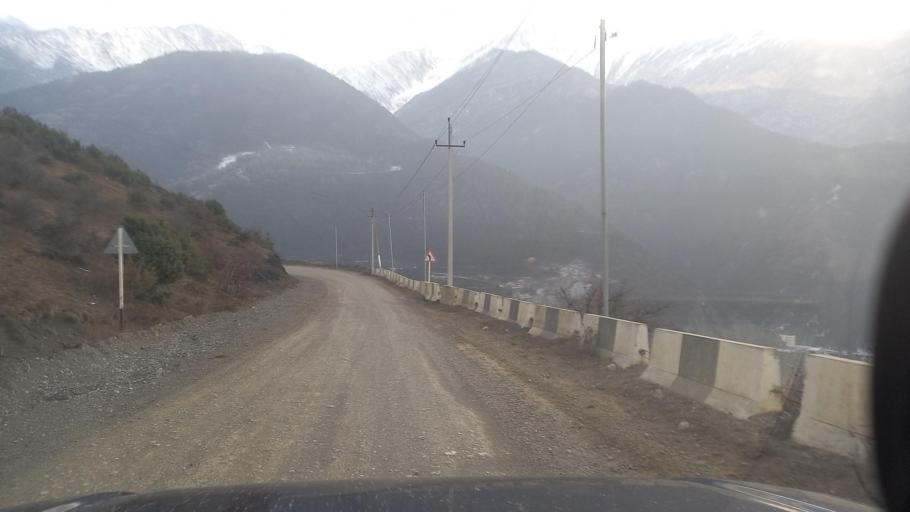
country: RU
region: Ingushetiya
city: Dzhayrakh
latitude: 42.8222
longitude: 44.7045
